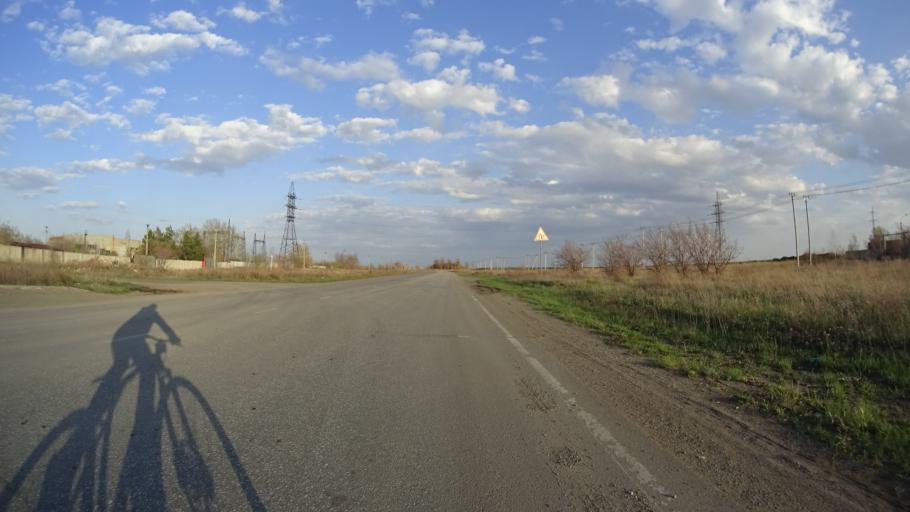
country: RU
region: Chelyabinsk
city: Troitsk
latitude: 54.0634
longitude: 61.5704
